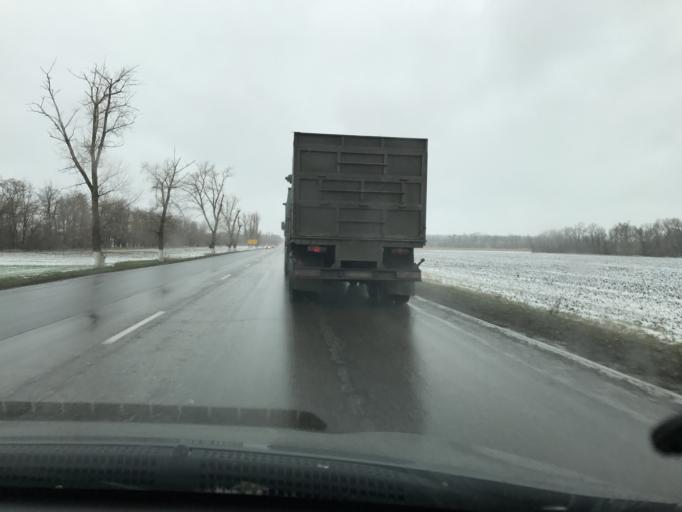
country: RU
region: Rostov
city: Zernograd
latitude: 46.8374
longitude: 40.2276
